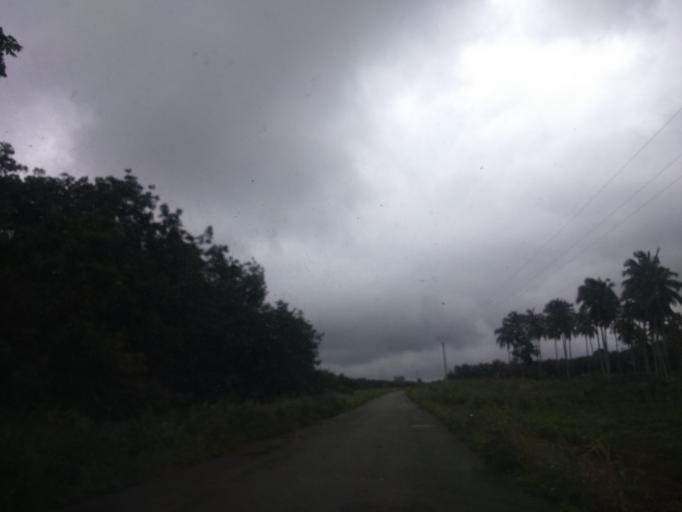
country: CI
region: Sud-Comoe
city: Adiake
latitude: 5.2948
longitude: -3.4430
